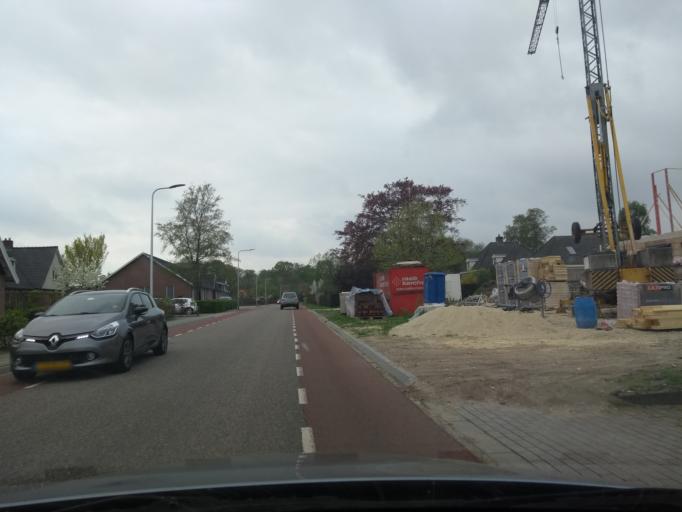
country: DE
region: Lower Saxony
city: Getelo
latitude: 52.4177
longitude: 6.9083
